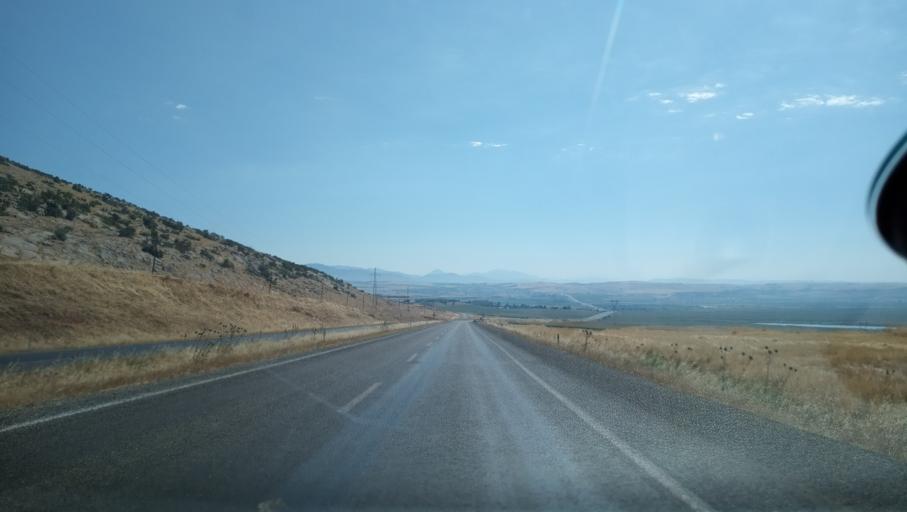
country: TR
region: Diyarbakir
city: Malabadi
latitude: 38.1267
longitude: 41.1672
